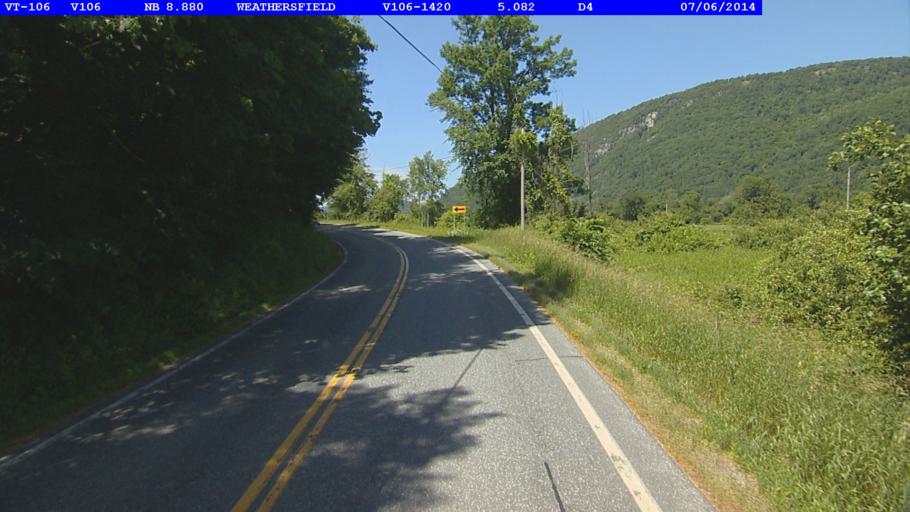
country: US
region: Vermont
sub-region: Windsor County
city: Springfield
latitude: 43.4113
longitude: -72.5132
